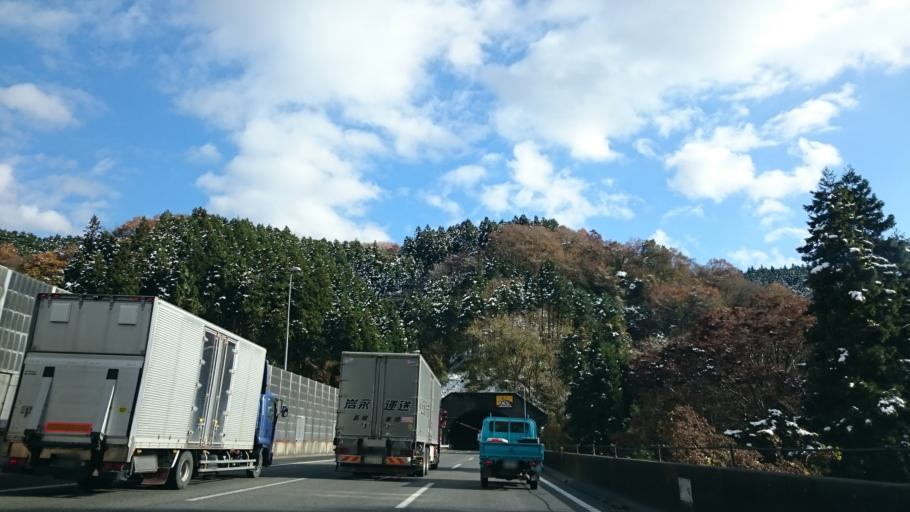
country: JP
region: Shizuoka
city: Gotemba
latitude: 35.3535
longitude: 138.9962
